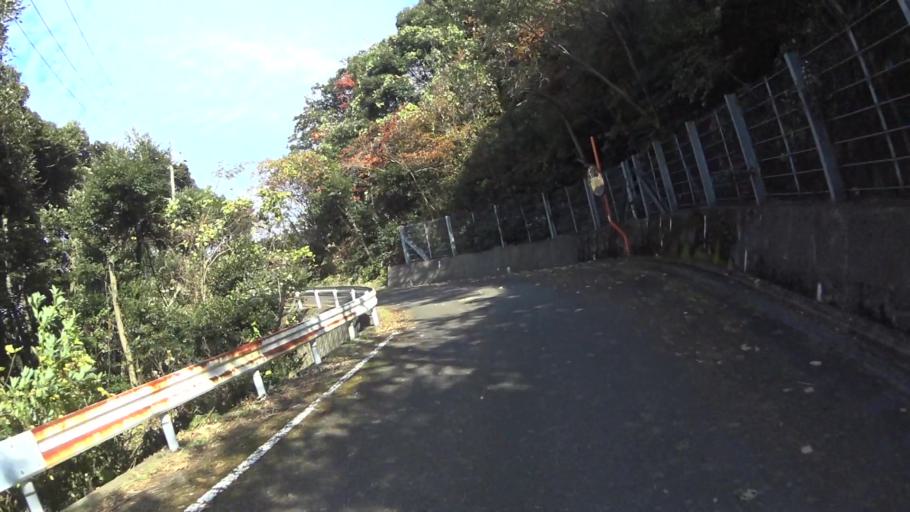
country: JP
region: Kyoto
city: Maizuru
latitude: 35.5610
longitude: 135.4043
